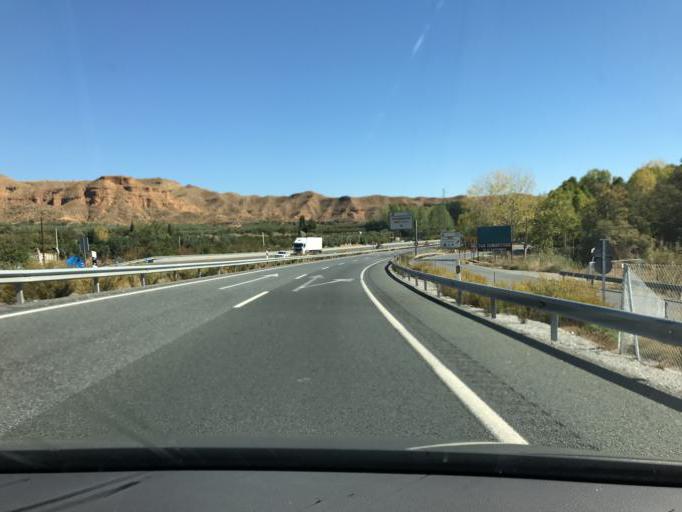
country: ES
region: Andalusia
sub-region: Provincia de Granada
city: Purullena
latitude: 37.3303
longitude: -3.2238
